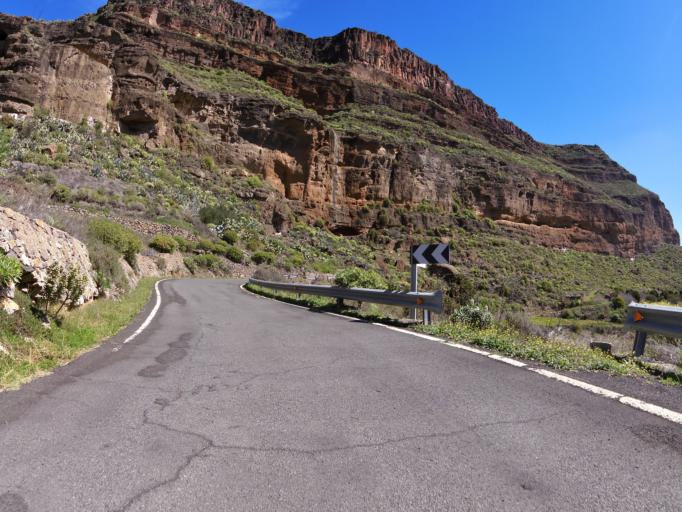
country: ES
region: Canary Islands
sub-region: Provincia de Las Palmas
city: Artenara
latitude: 28.0012
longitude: -15.6898
